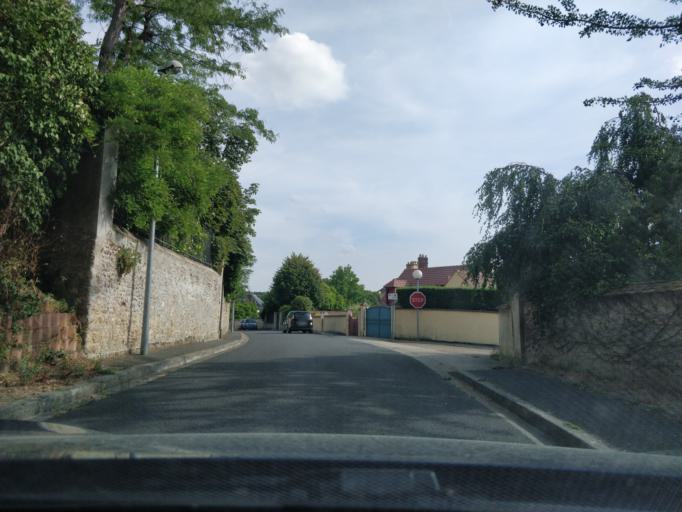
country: FR
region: Ile-de-France
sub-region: Departement de l'Essonne
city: Briis-sous-Forges
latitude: 48.6258
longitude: 2.1209
